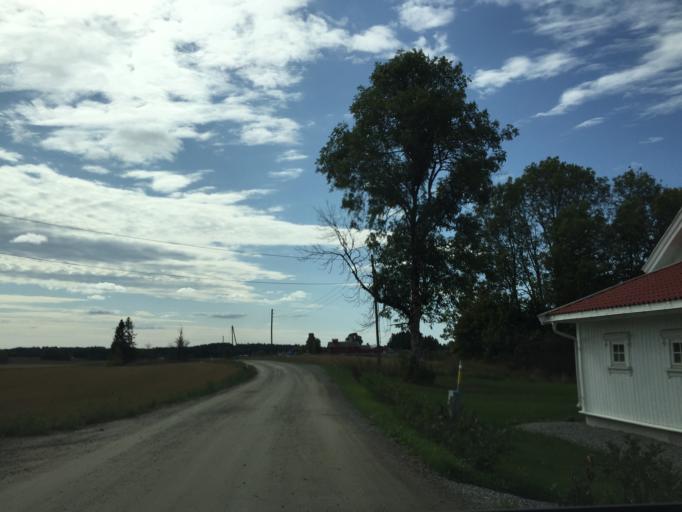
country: NO
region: Ostfold
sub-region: Hobol
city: Elvestad
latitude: 59.6418
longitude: 10.8880
